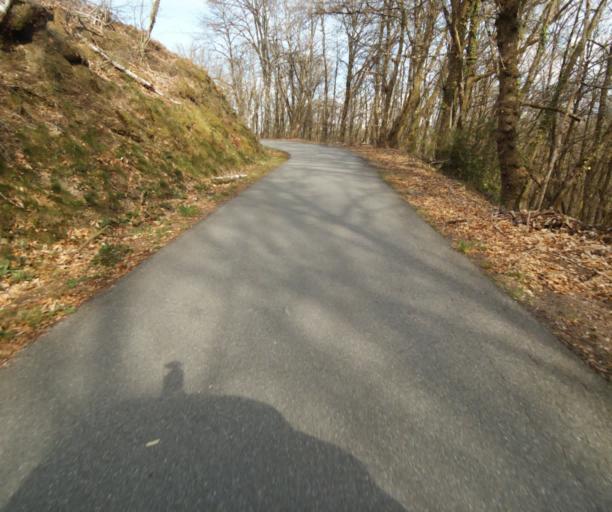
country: FR
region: Limousin
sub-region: Departement de la Correze
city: Correze
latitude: 45.3436
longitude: 1.8481
